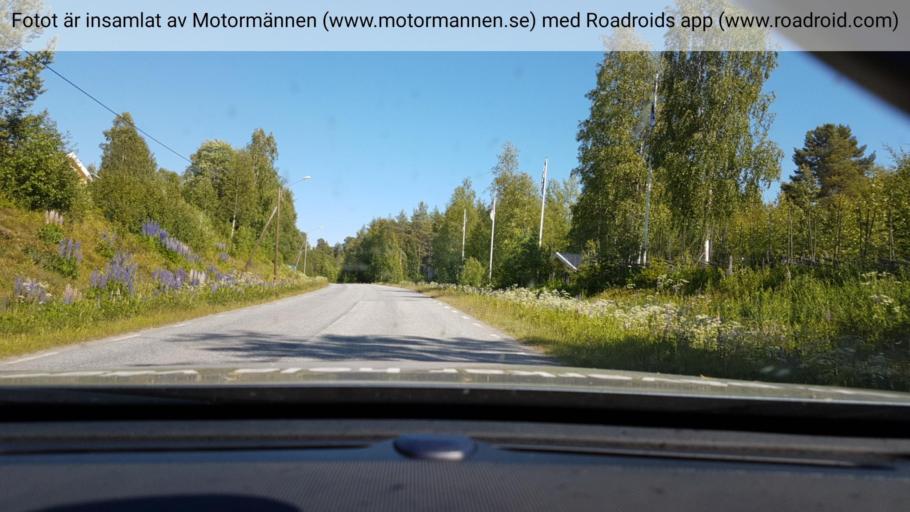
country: SE
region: Vaesterbotten
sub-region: Vilhelmina Kommun
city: Vilhelmina
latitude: 64.6500
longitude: 16.5892
